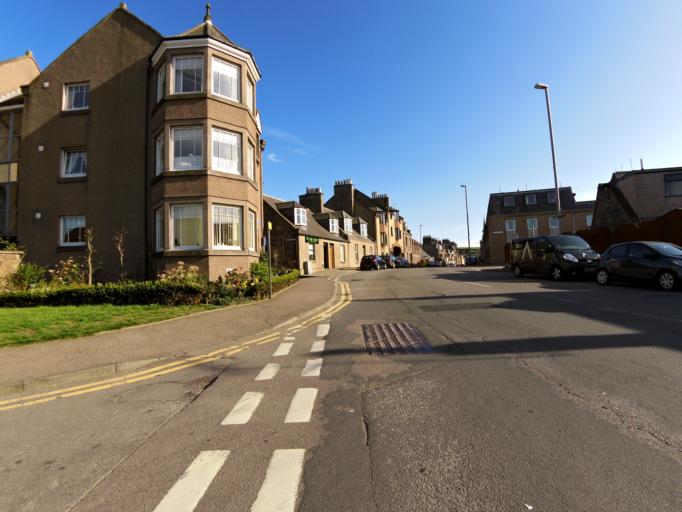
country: GB
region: Scotland
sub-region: Aberdeenshire
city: Stonehaven
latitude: 56.9660
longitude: -2.2084
